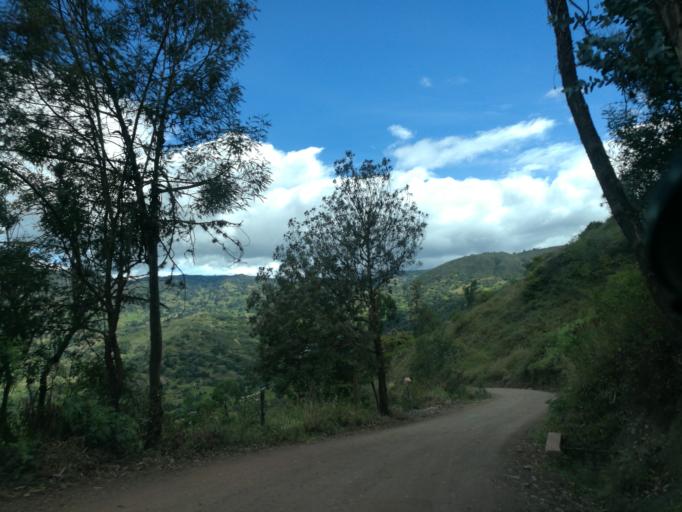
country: CO
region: Boyaca
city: Susacon
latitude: 6.1226
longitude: -72.7112
